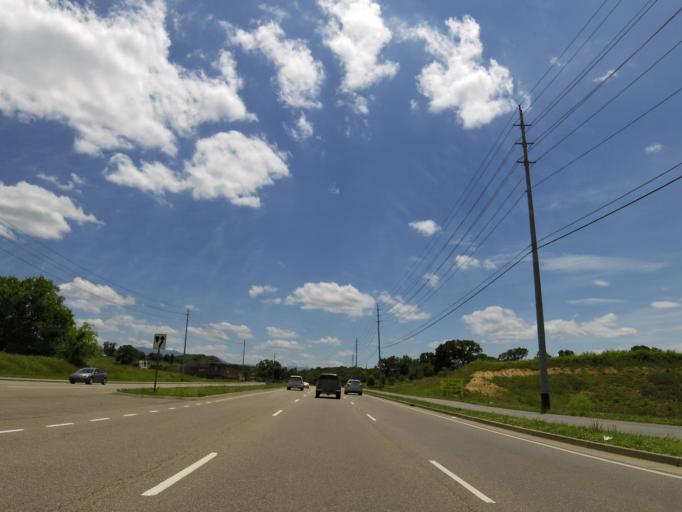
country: US
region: Tennessee
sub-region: Sevier County
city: Sevierville
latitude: 35.8488
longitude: -83.5429
